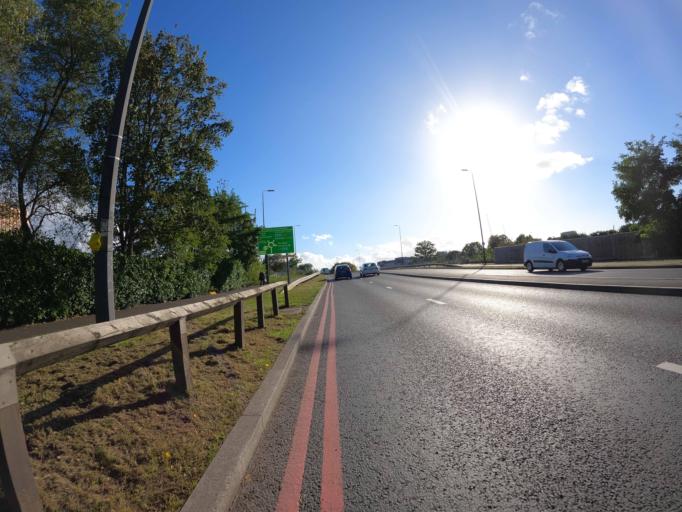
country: GB
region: England
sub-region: Greater London
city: Acton
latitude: 51.4948
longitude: -0.2823
